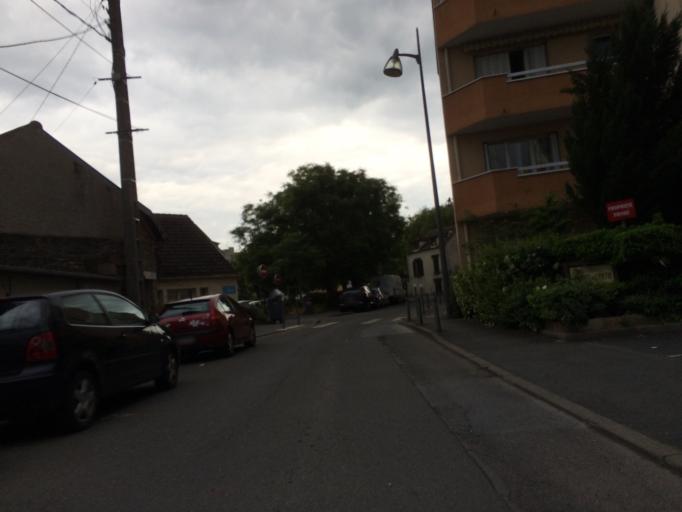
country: FR
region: Ile-de-France
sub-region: Departement de l'Essonne
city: Longjumeau
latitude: 48.6950
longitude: 2.2934
